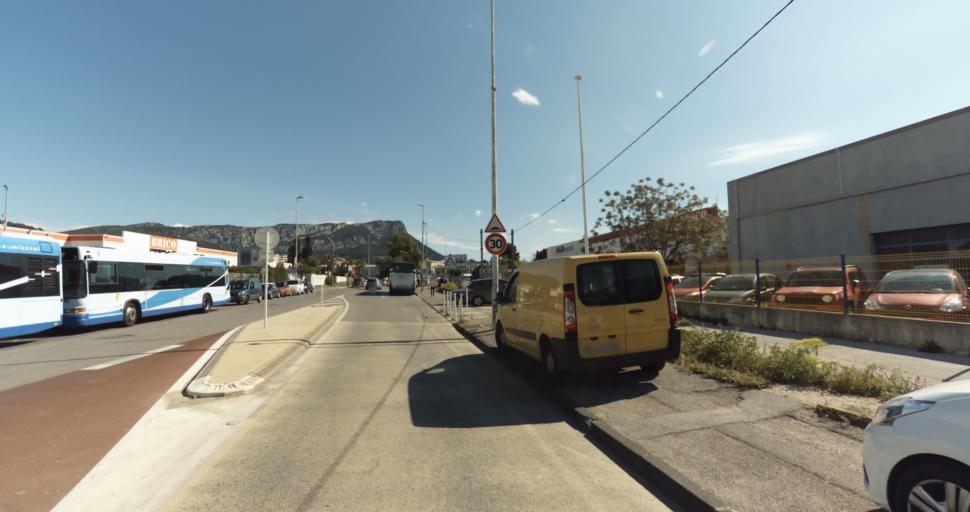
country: FR
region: Provence-Alpes-Cote d'Azur
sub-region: Departement du Var
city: La Valette-du-Var
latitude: 43.1259
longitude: 5.9759
